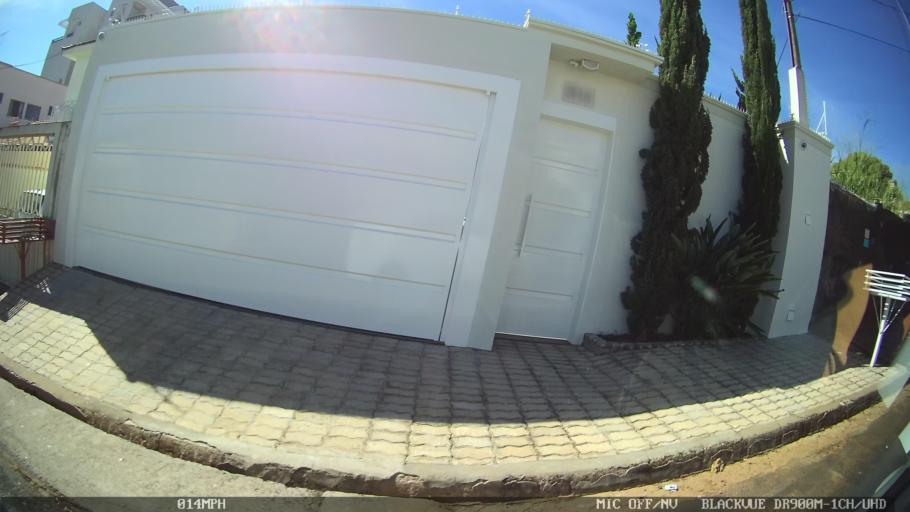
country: BR
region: Sao Paulo
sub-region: Franca
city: Franca
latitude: -20.5541
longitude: -47.4004
